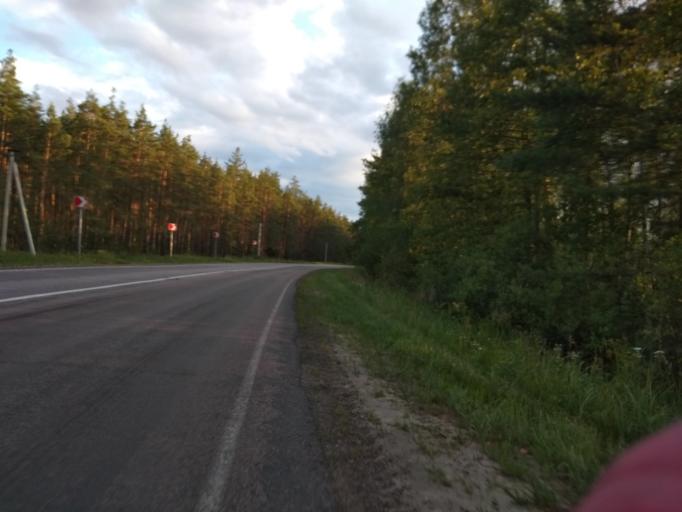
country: RU
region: Moskovskaya
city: Misheronskiy
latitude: 55.6273
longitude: 39.7393
